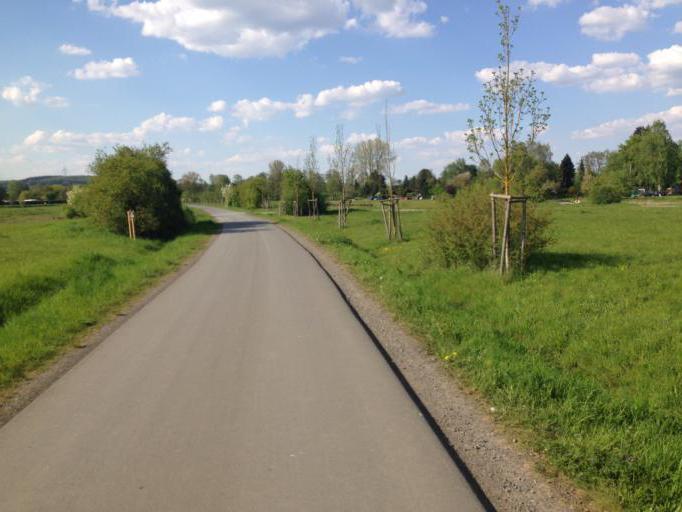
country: DE
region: Hesse
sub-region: Regierungsbezirk Giessen
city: Giessen
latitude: 50.6041
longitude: 8.6711
